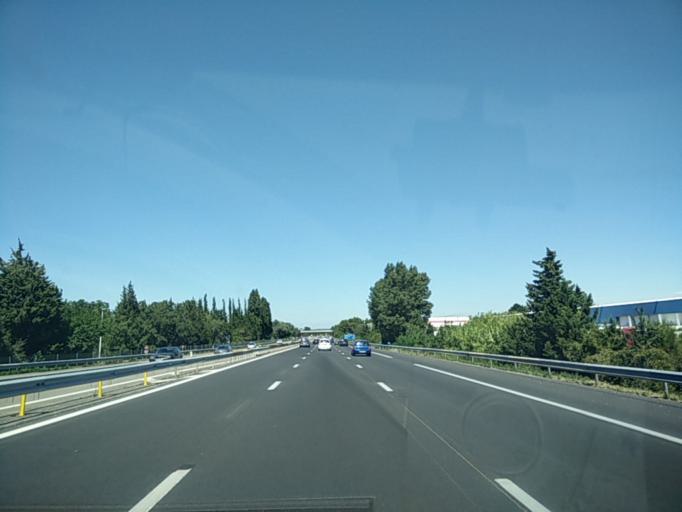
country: FR
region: Provence-Alpes-Cote d'Azur
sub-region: Departement du Vaucluse
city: Vedene
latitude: 43.9865
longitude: 4.8905
